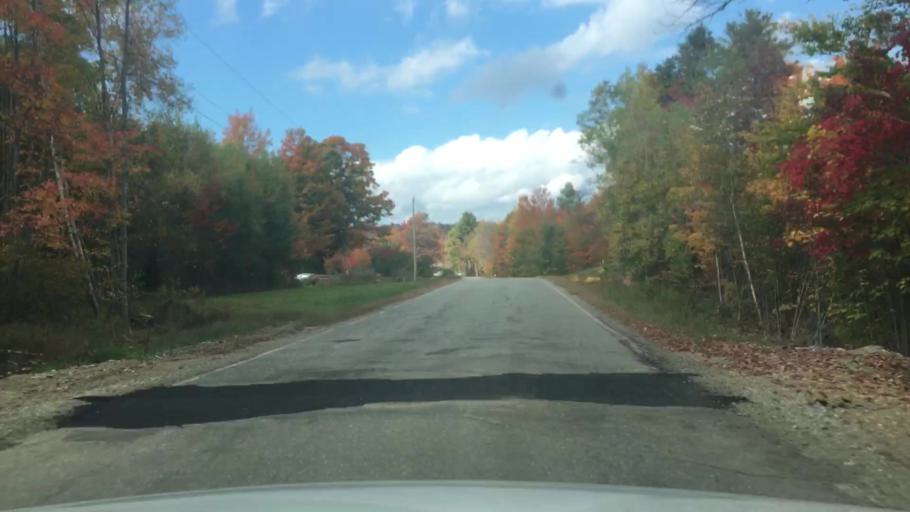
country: US
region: Maine
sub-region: Knox County
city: Washington
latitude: 44.3320
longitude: -69.3699
